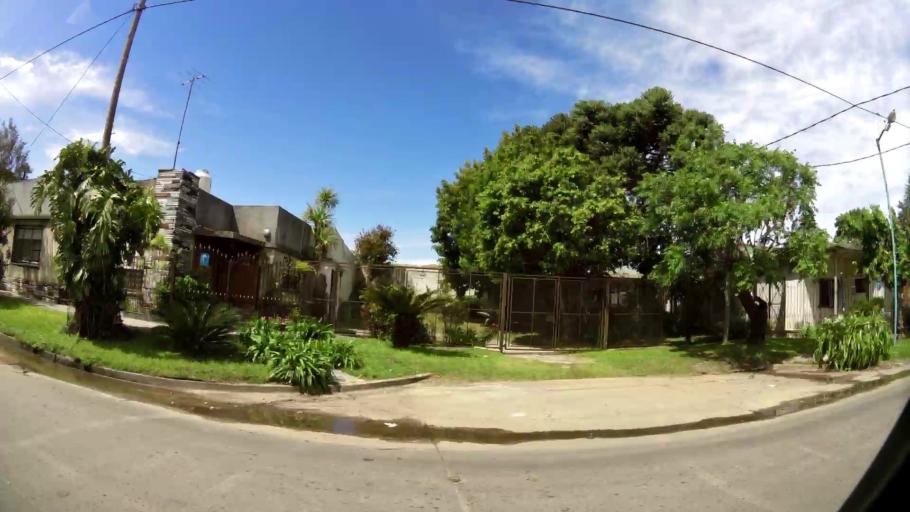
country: AR
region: Buenos Aires
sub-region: Partido de Quilmes
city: Quilmes
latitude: -34.7552
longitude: -58.2956
